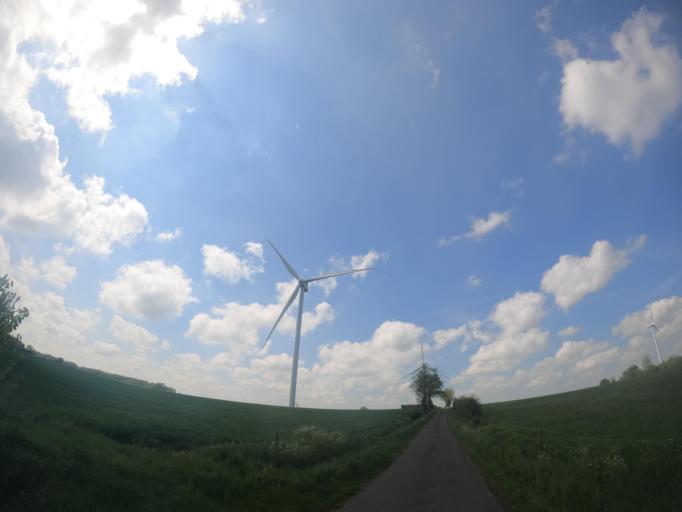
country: FR
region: Poitou-Charentes
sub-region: Departement des Deux-Sevres
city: Saint-Varent
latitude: 46.8593
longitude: -0.2154
